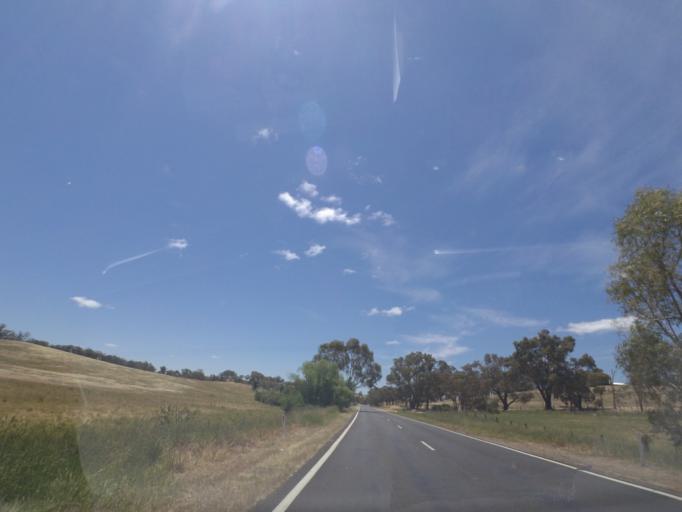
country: AU
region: Victoria
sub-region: Mount Alexander
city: Castlemaine
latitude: -37.1581
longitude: 144.1595
